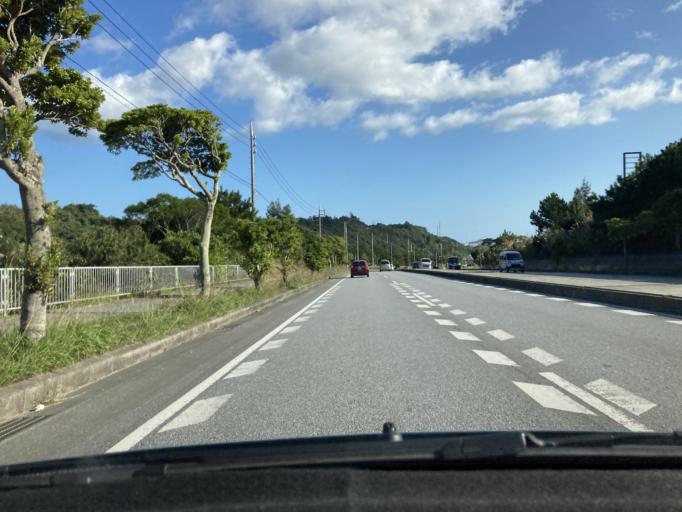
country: JP
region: Okinawa
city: Ishikawa
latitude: 26.4019
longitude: 127.8271
